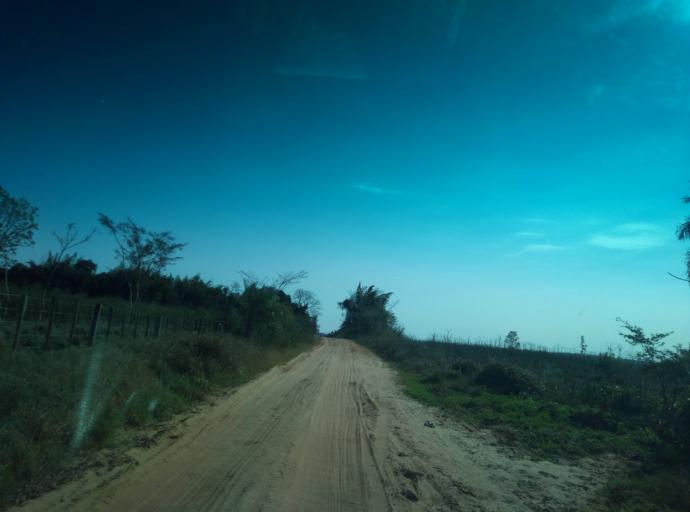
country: PY
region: Caaguazu
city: Doctor Cecilio Baez
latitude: -25.1649
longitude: -56.2146
